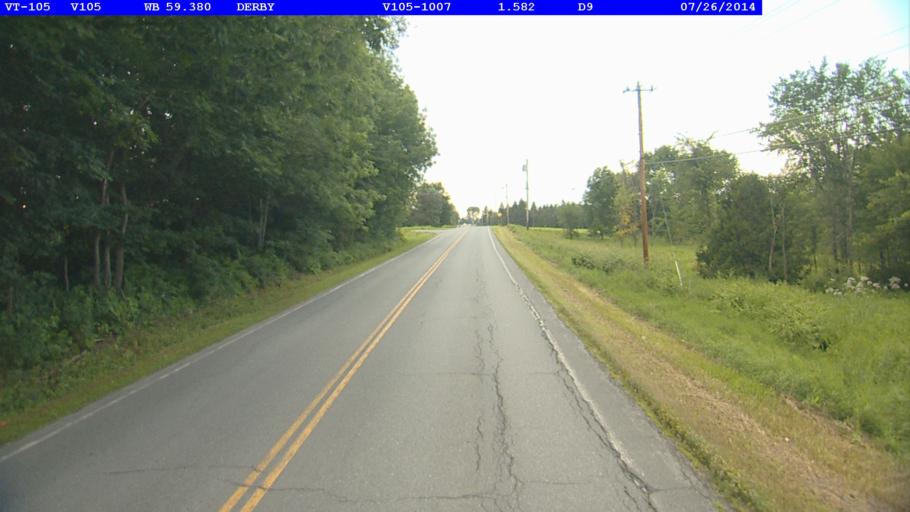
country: US
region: Vermont
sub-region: Orleans County
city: Newport
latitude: 44.9359
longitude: -72.1222
